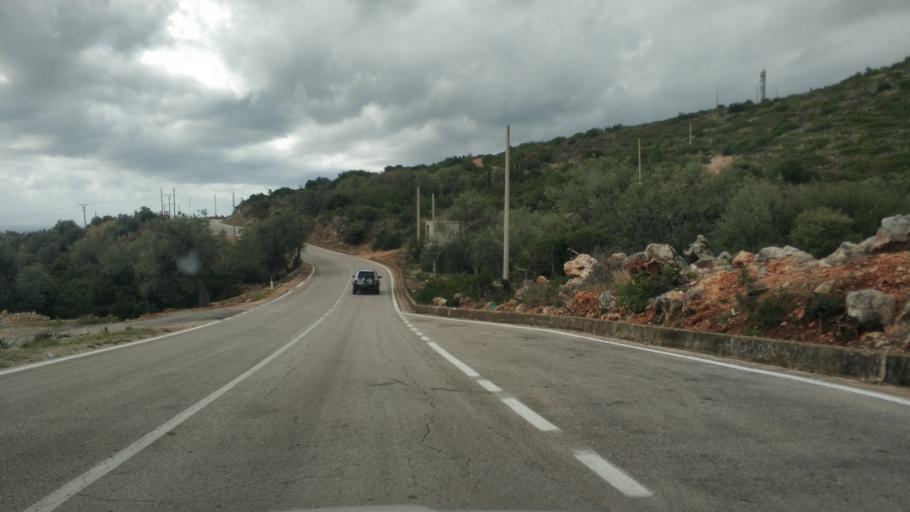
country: AL
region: Vlore
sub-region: Rrethi i Vlores
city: Vranisht
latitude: 40.1447
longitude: 19.6495
